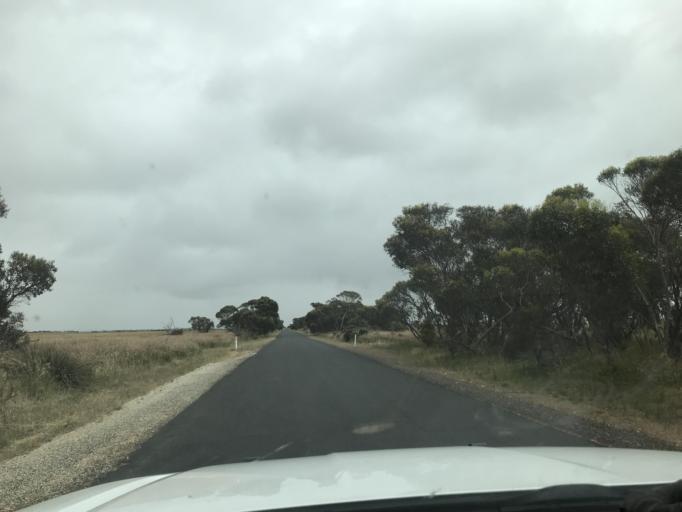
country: AU
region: South Australia
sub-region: Tatiara
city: Bordertown
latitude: -36.1187
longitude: 141.0499
